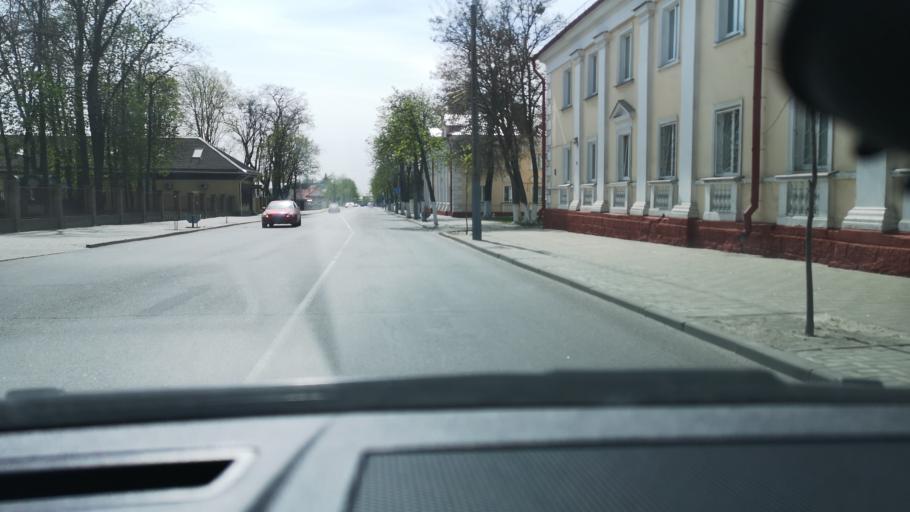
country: BY
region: Gomel
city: Gomel
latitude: 52.4179
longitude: 31.0083
